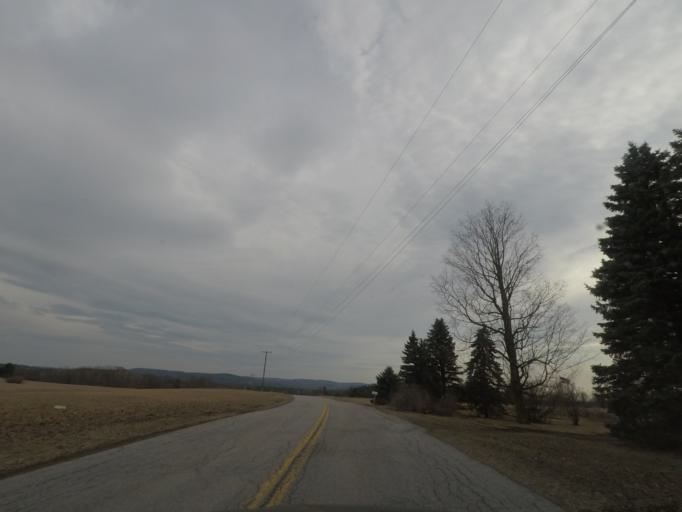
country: US
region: New York
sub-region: Rensselaer County
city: Hoosick Falls
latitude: 42.8902
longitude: -73.4429
